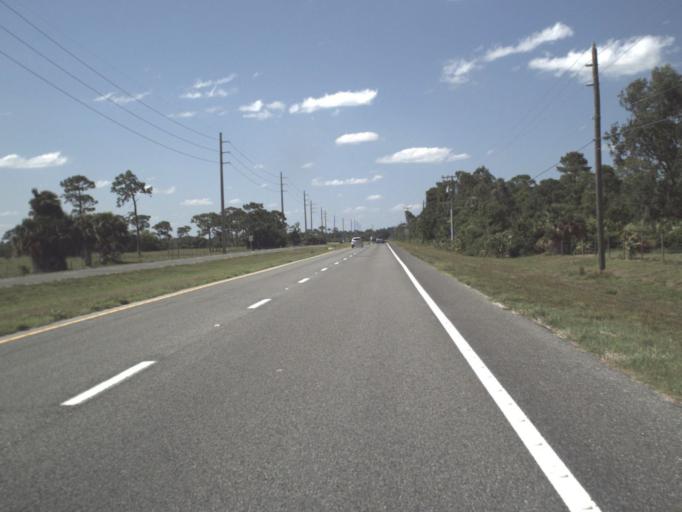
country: US
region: Florida
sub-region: Volusia County
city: Oak Hill
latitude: 28.7742
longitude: -80.8798
